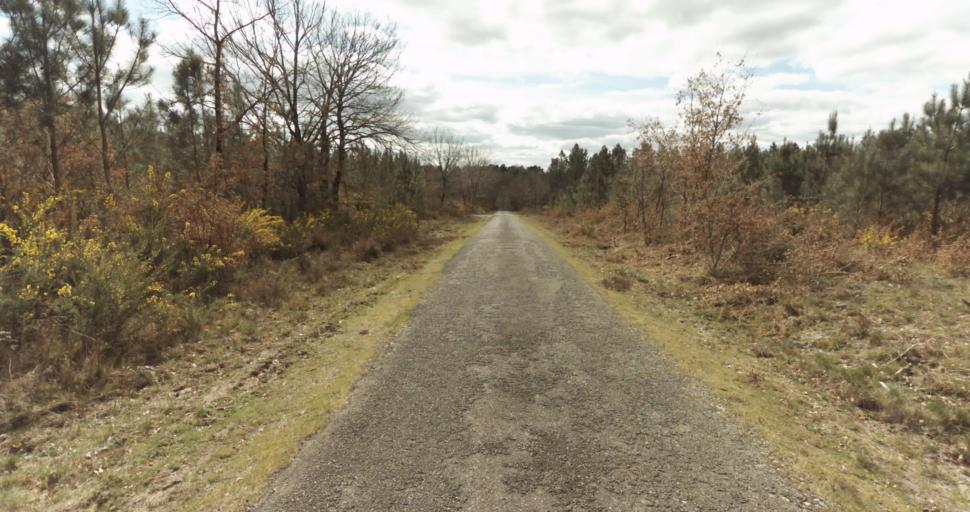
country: FR
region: Aquitaine
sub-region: Departement des Landes
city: Roquefort
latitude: 44.0900
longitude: -0.4408
